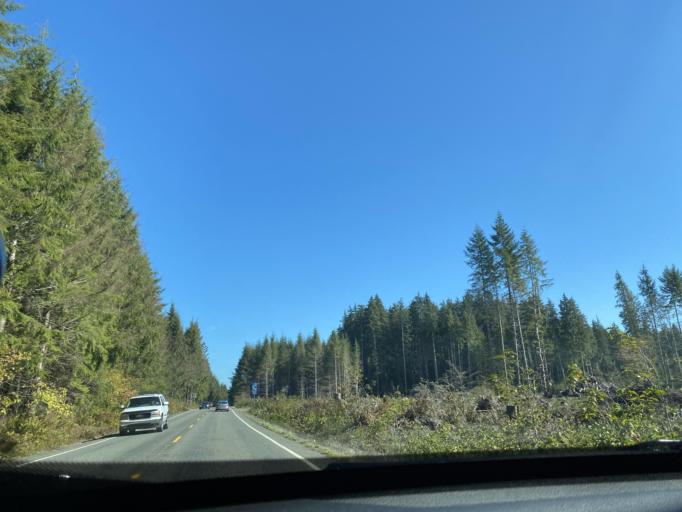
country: US
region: Washington
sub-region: Clallam County
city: Forks
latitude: 47.9186
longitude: -124.5198
